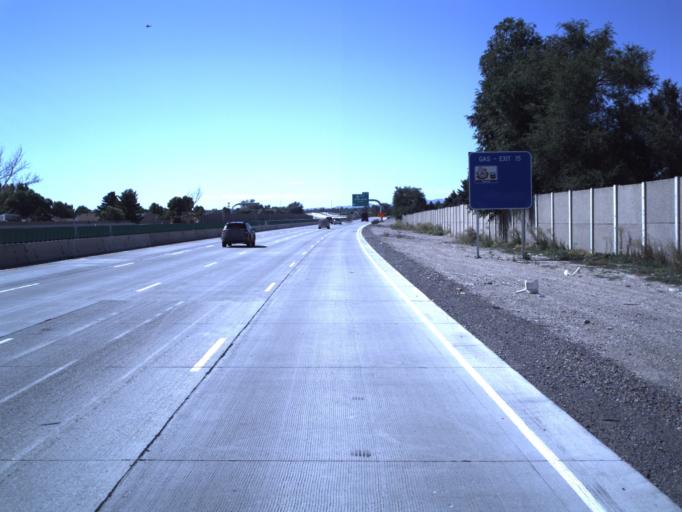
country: US
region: Utah
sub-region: Salt Lake County
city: Taylorsville
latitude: 40.6817
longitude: -111.9518
